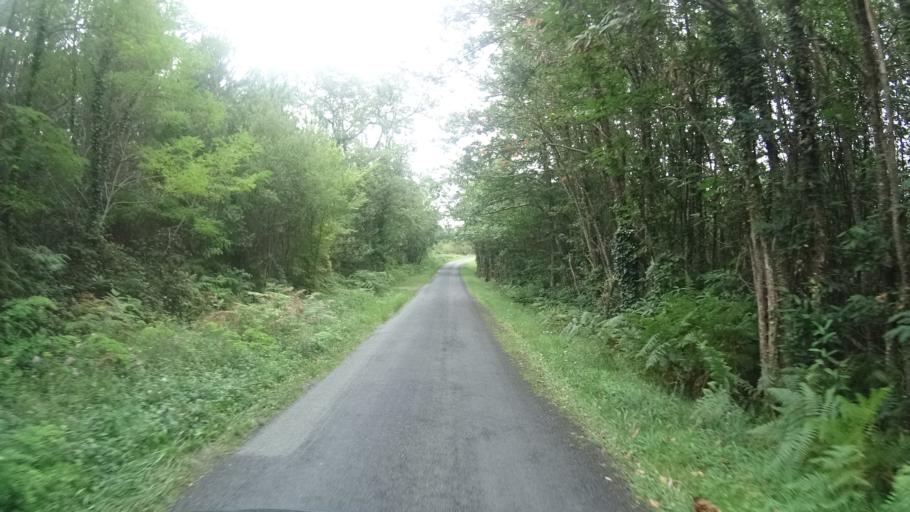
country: FR
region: Aquitaine
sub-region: Departement de la Dordogne
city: Neuvic
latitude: 45.0100
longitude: 0.5502
